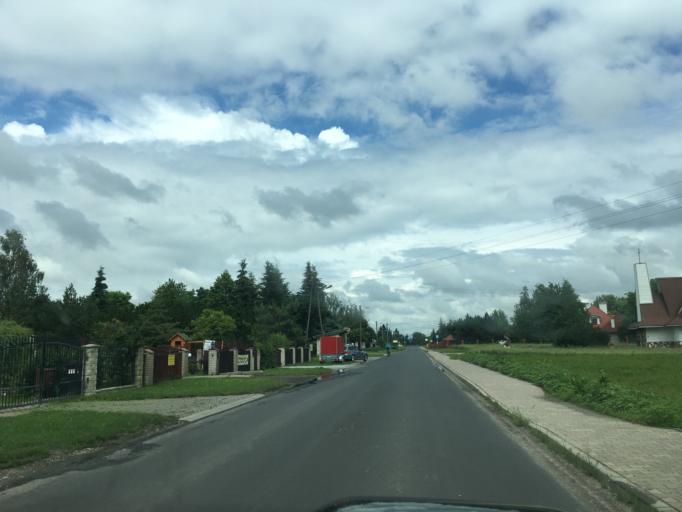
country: PL
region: Lublin Voivodeship
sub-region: Powiat swidnicki
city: Swidnik
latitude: 51.2003
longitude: 22.7306
